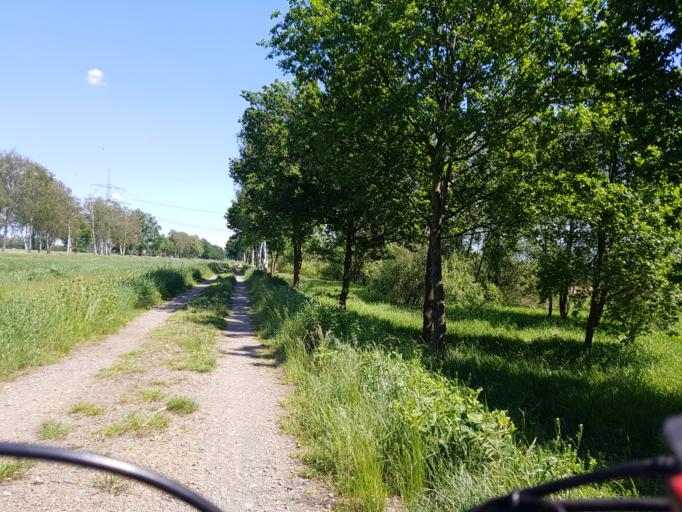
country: DE
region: Brandenburg
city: Merzdorf
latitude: 51.4304
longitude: 13.5473
